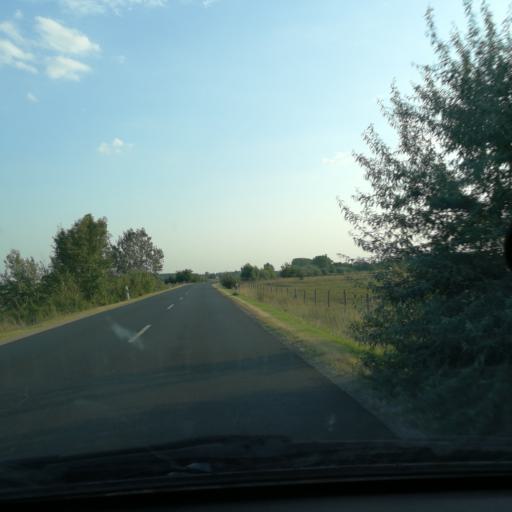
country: HU
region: Bacs-Kiskun
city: Kiskunmajsa
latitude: 46.4779
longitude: 19.7083
